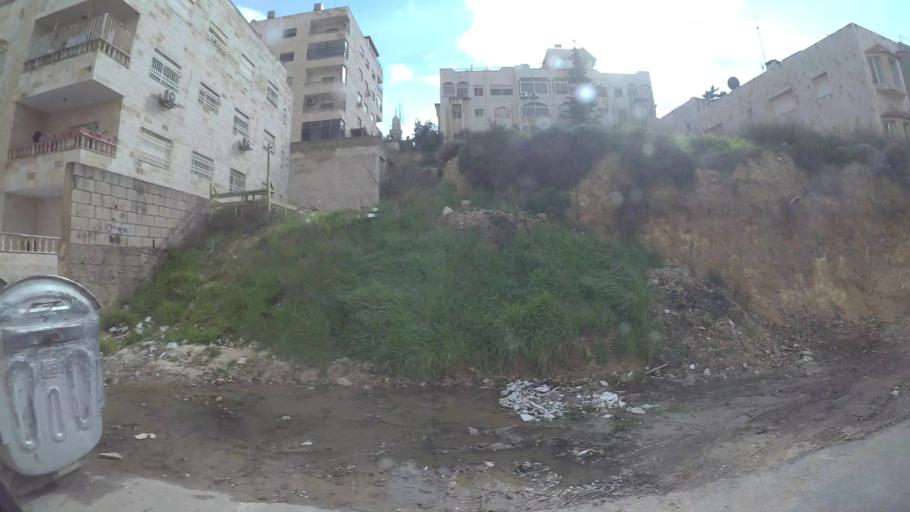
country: JO
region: Amman
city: Al Jubayhah
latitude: 32.0192
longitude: 35.8588
